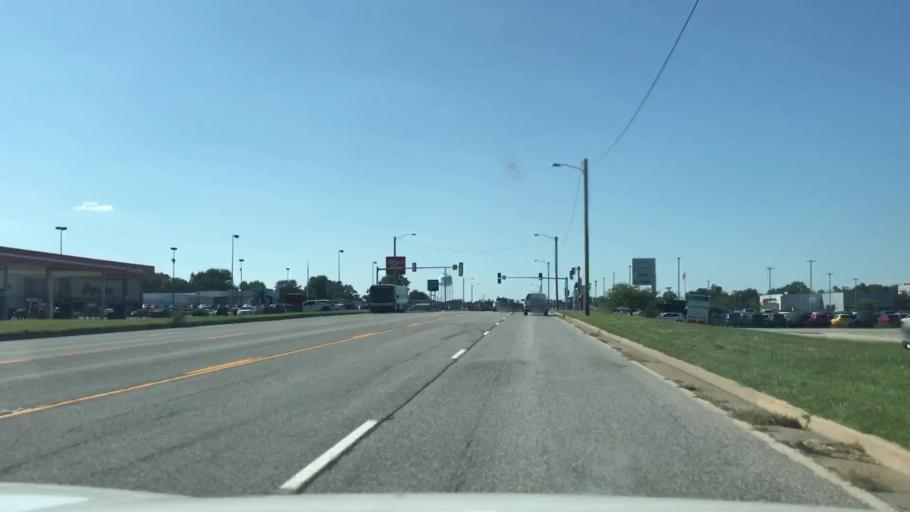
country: US
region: Illinois
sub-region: Madison County
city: Roxana
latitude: 38.8566
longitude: -90.0645
